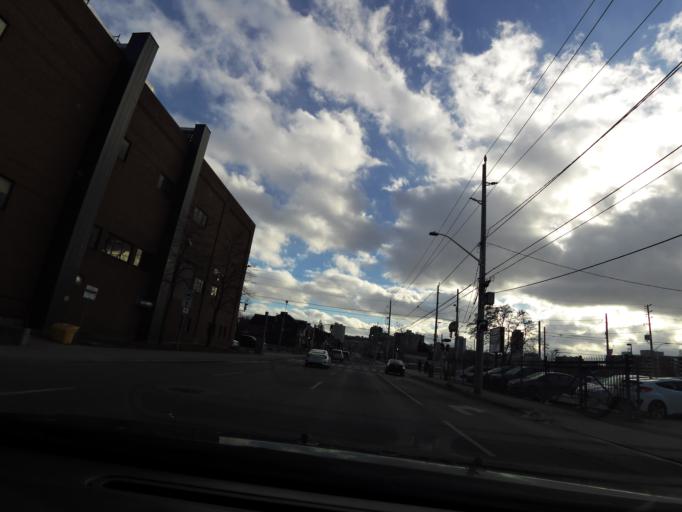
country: CA
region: Ontario
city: Hamilton
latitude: 43.2622
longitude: -79.8557
